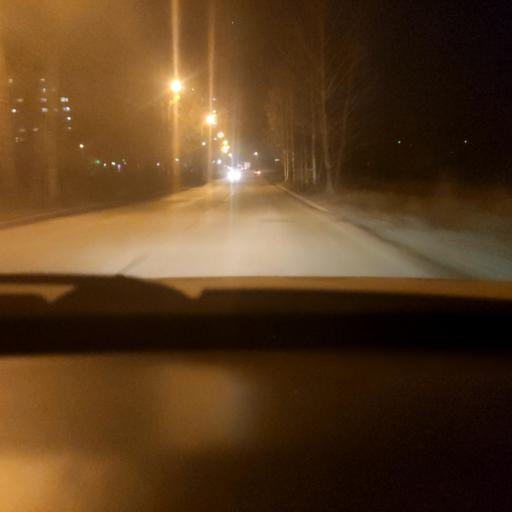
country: RU
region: Perm
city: Polazna
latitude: 58.1331
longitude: 56.3907
